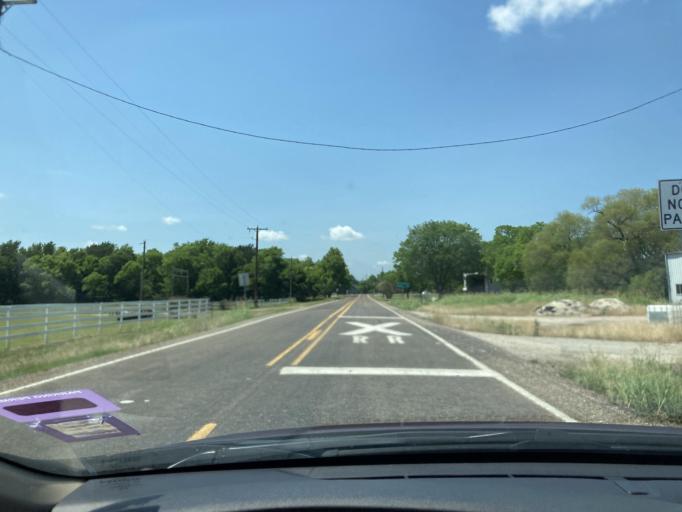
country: US
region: Texas
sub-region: Navarro County
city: Kerens
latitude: 32.1151
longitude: -96.3273
